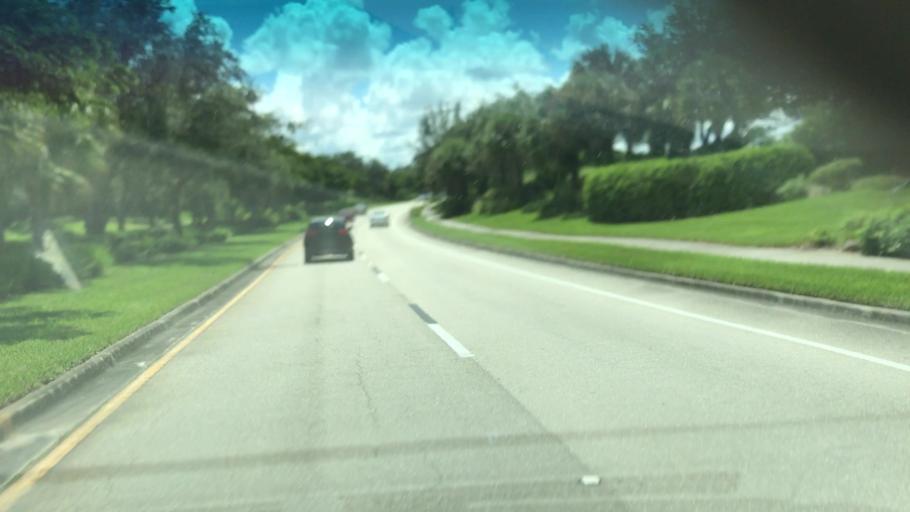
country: US
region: Florida
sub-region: Lee County
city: Estero
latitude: 26.4118
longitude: -81.7844
